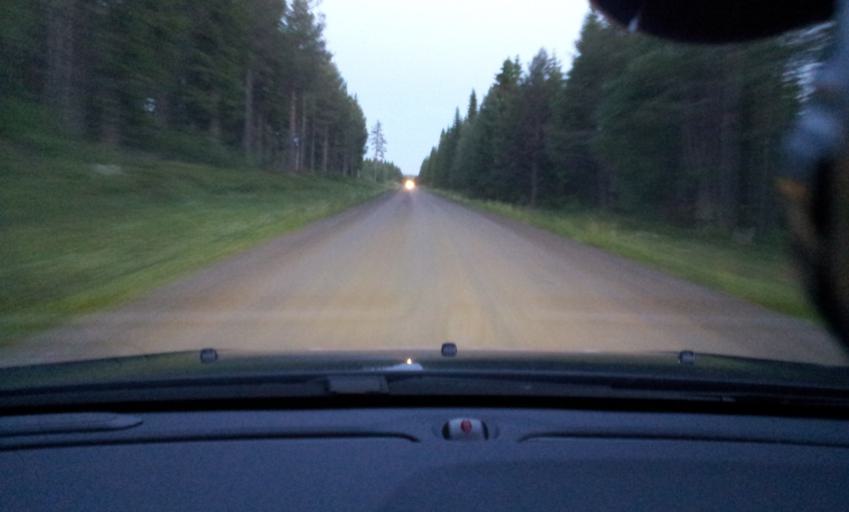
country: SE
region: Jaemtland
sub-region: Braecke Kommun
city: Braecke
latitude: 62.7472
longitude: 15.6419
